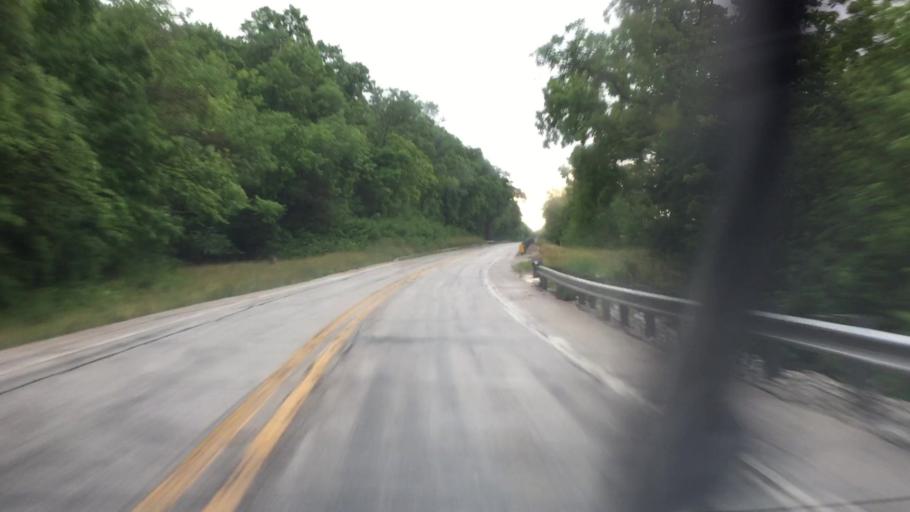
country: US
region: Iowa
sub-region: Lee County
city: Keokuk
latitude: 40.4647
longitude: -91.3628
